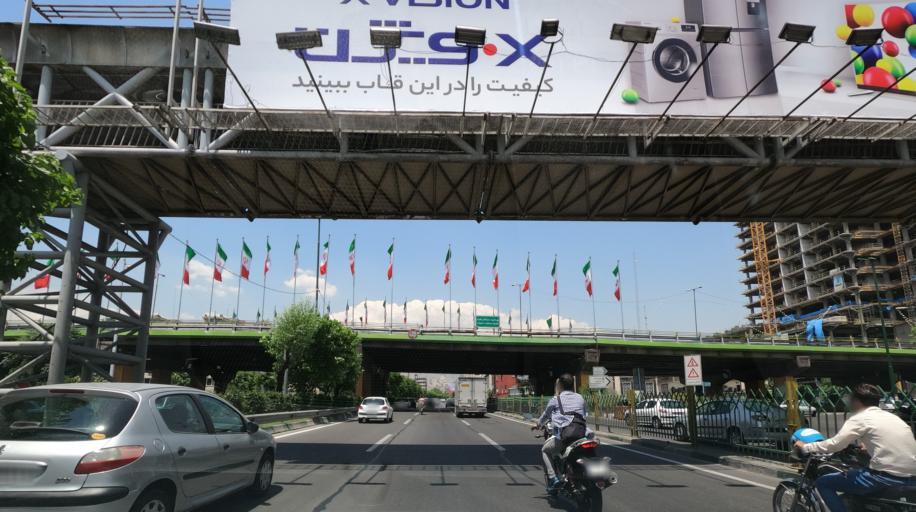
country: IR
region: Tehran
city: Tajrish
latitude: 35.7612
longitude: 51.4208
